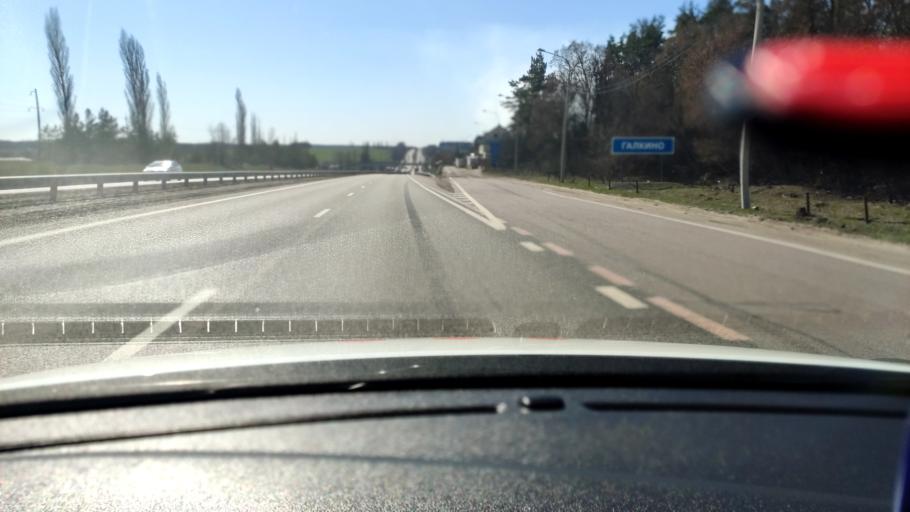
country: RU
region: Voronezj
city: Ramon'
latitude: 51.9489
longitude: 39.2223
